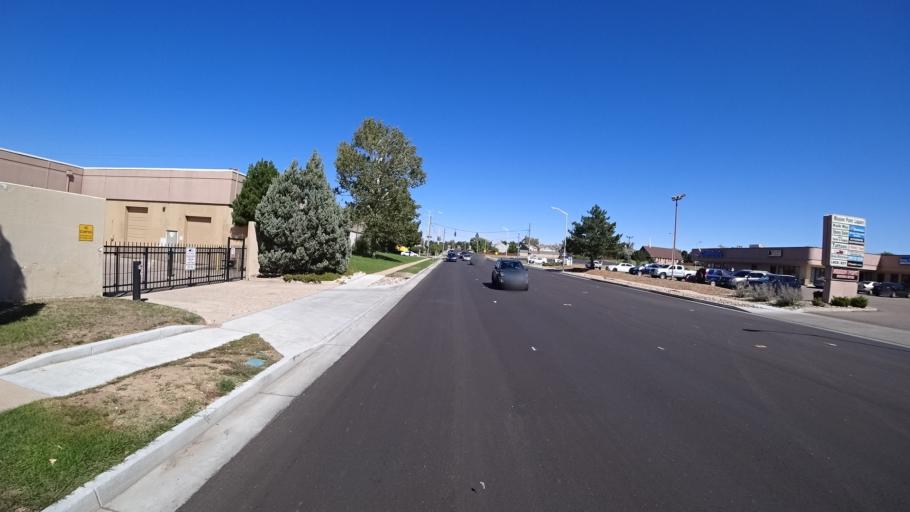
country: US
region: Colorado
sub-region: El Paso County
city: Stratmoor
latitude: 38.7881
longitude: -104.7542
